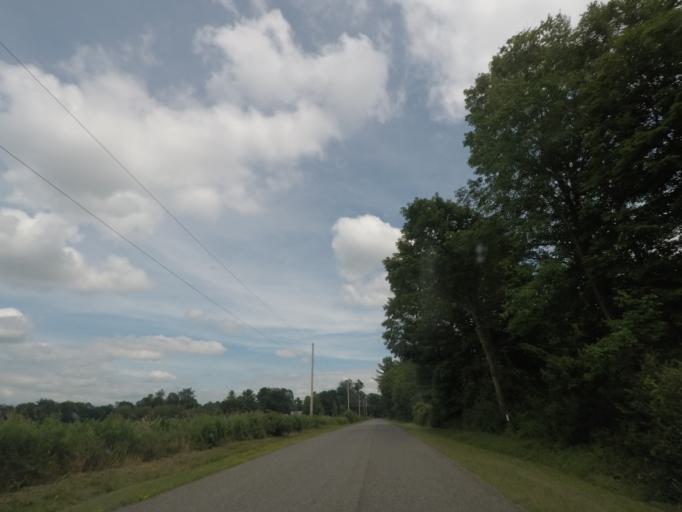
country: US
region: New York
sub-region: Saratoga County
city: Stillwater
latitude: 43.0101
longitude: -73.6302
